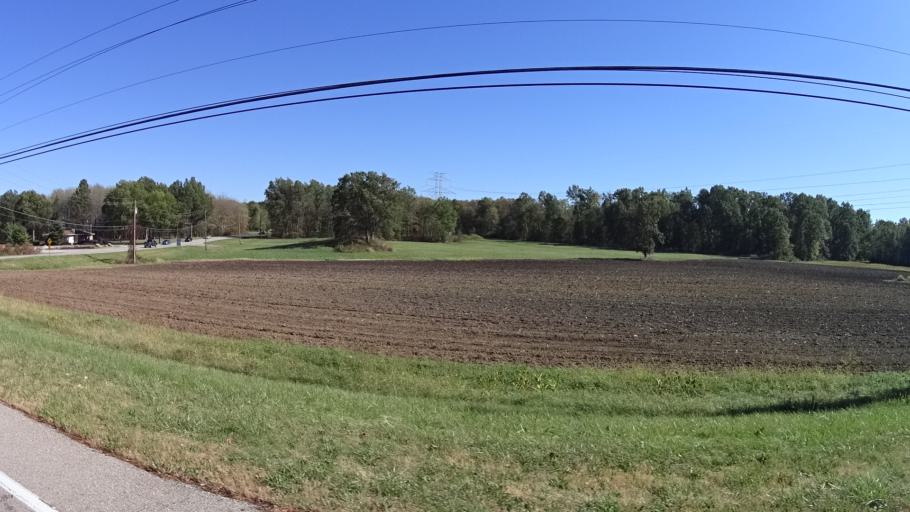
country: US
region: Ohio
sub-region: Lorain County
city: Lorain
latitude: 41.4092
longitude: -82.1687
